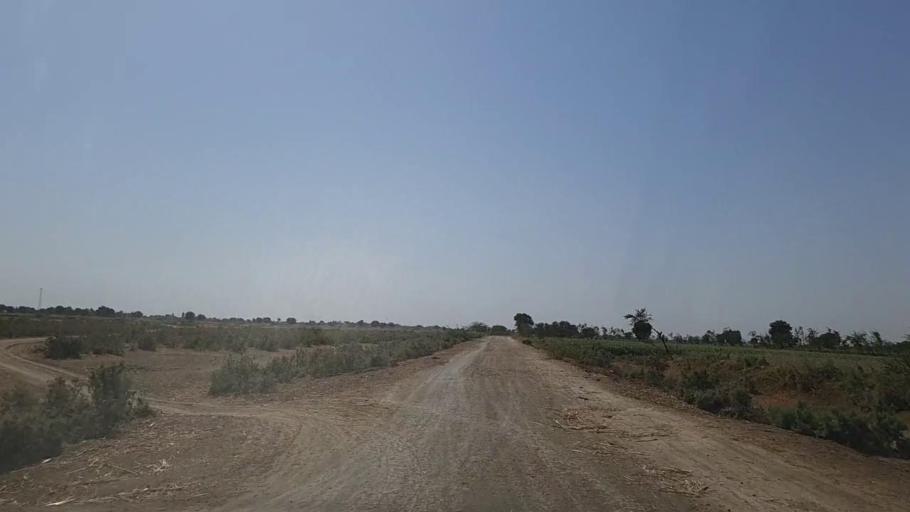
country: PK
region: Sindh
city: Samaro
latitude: 25.2308
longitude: 69.4081
